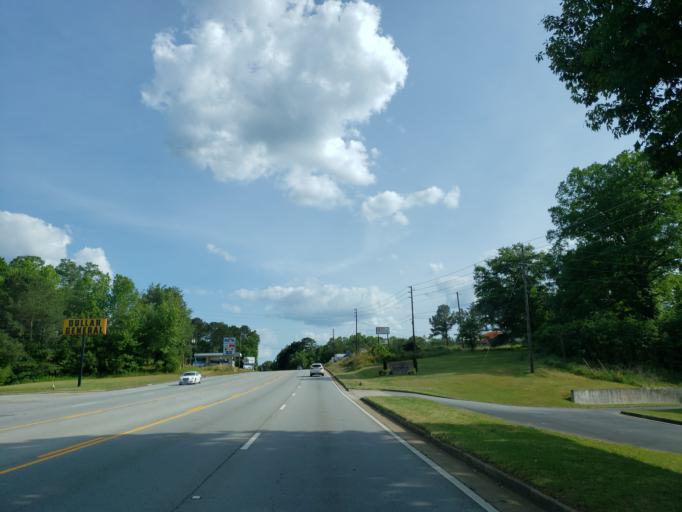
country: US
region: Georgia
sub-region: Carroll County
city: Carrollton
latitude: 33.5965
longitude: -85.0794
